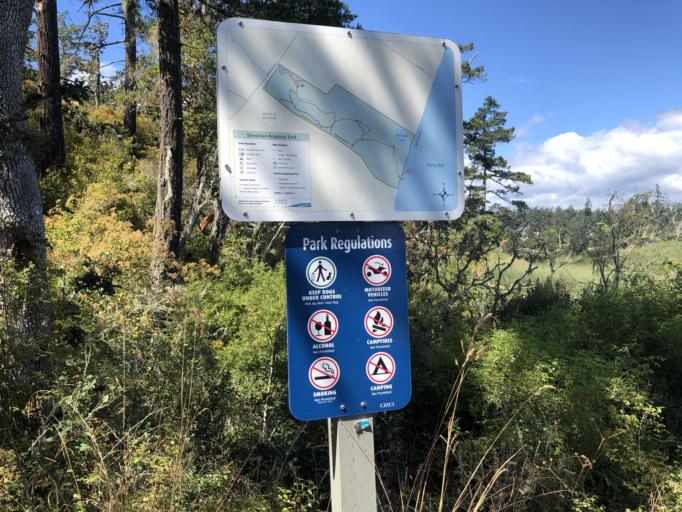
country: CA
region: British Columbia
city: Metchosin
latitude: 48.3623
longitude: -123.5348
